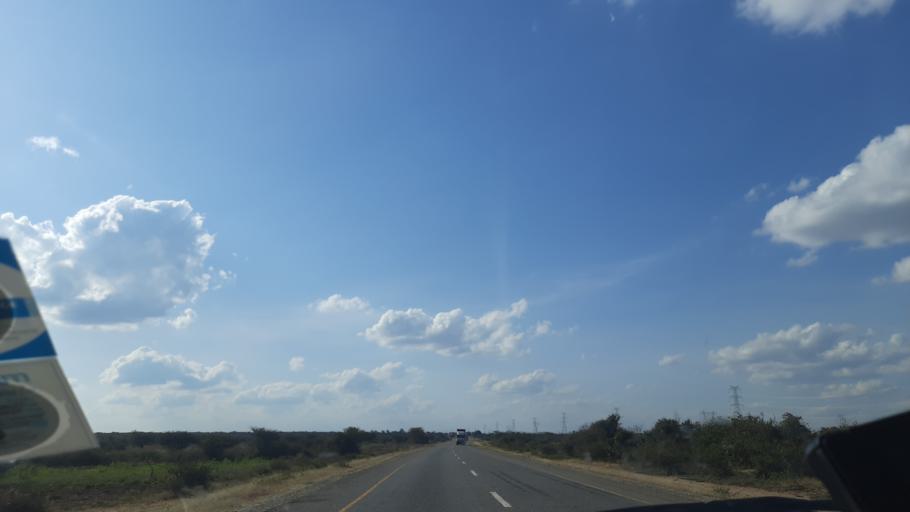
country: TZ
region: Singida
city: Ikungi
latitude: -5.1872
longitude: 34.7829
